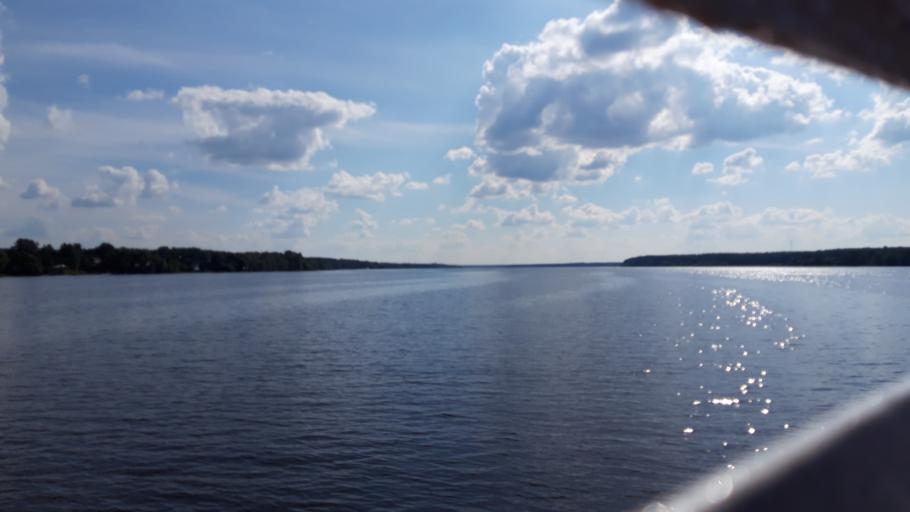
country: RU
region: Tverskaya
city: Konakovo
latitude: 56.6684
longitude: 36.6591
